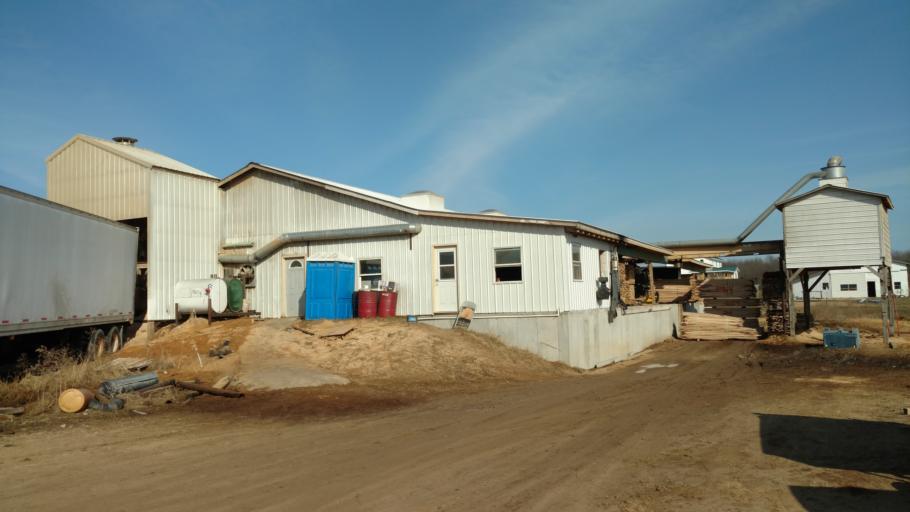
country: US
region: Wisconsin
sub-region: Vernon County
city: Hillsboro
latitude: 43.6207
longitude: -90.4475
